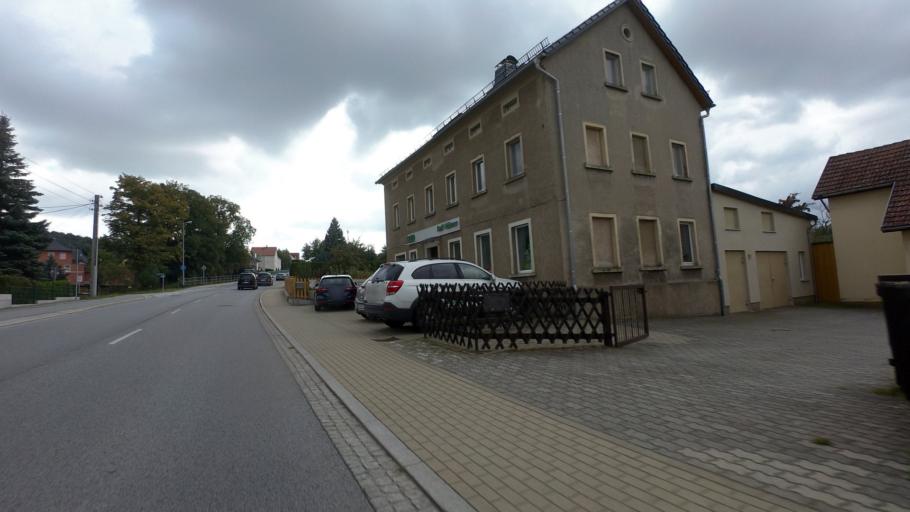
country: DE
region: Saxony
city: Grosspostwitz
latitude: 51.1391
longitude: 14.4416
